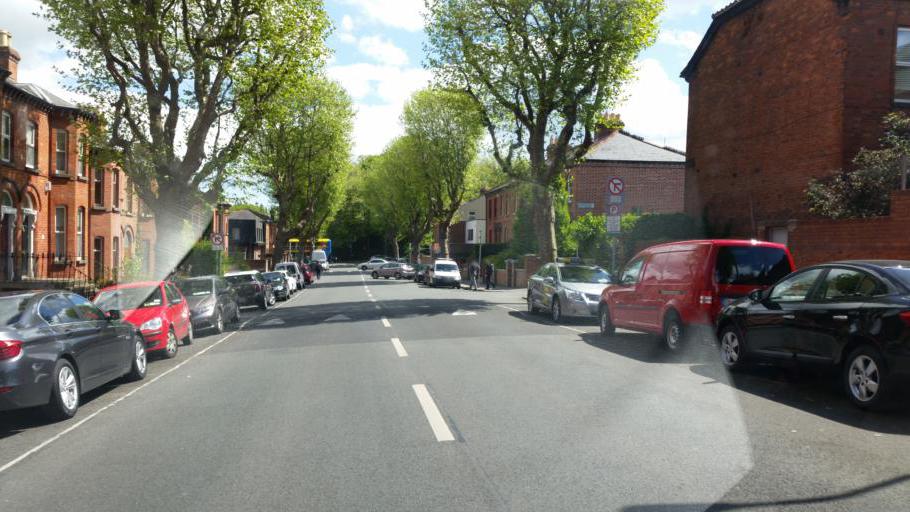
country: IE
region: Leinster
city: Drumcondra
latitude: 53.3672
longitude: -6.2575
